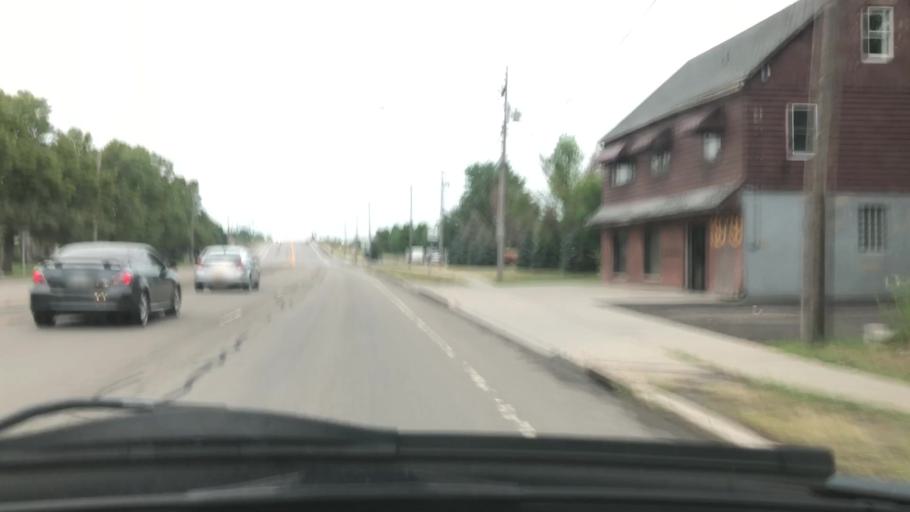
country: US
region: New York
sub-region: Erie County
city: Sloan
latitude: 42.8965
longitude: -78.7842
